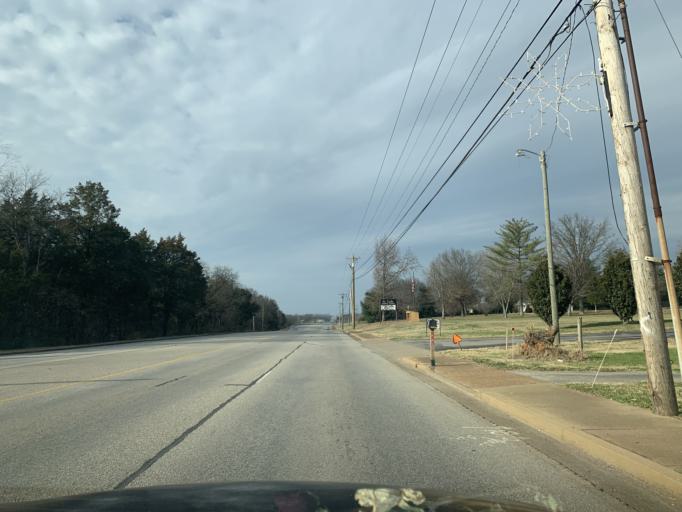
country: US
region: Tennessee
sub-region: Rutherford County
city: Smyrna
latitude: 35.9499
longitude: -86.5100
